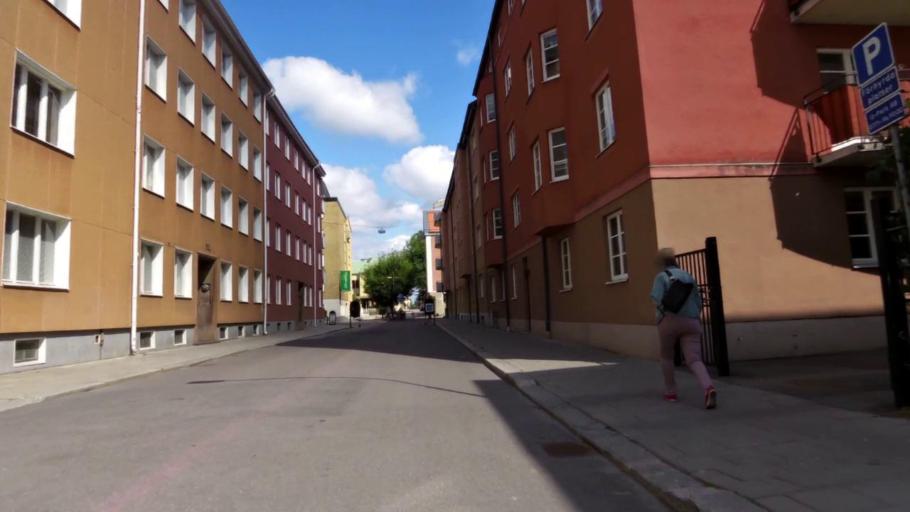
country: SE
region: OEstergoetland
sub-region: Linkopings Kommun
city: Linkoping
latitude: 58.4079
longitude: 15.6237
